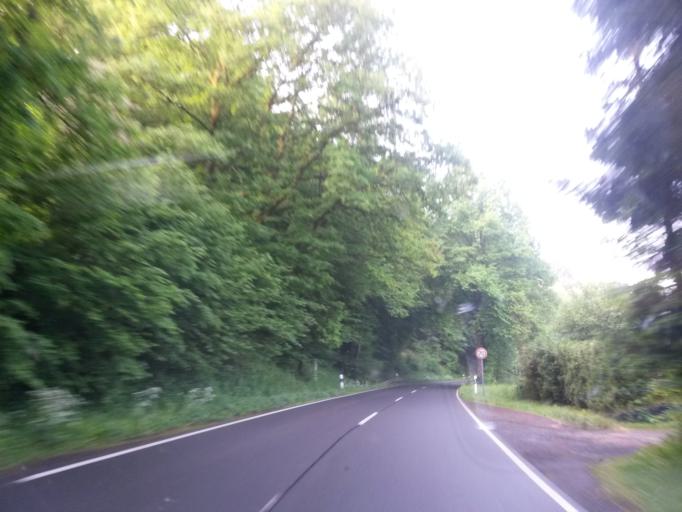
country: DE
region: North Rhine-Westphalia
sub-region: Regierungsbezirk Koln
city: Much
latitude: 50.8649
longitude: 7.3406
